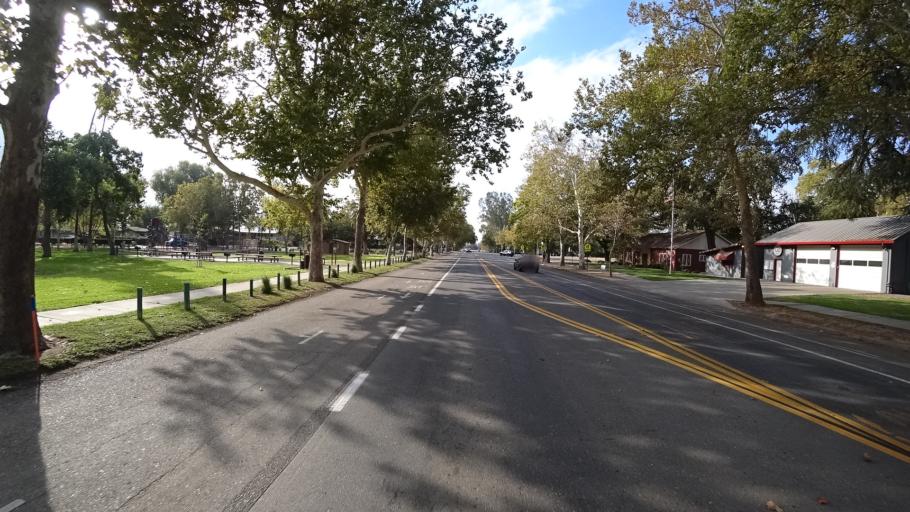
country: US
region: California
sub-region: Yolo County
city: Esparto
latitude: 38.6936
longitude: -122.0165
